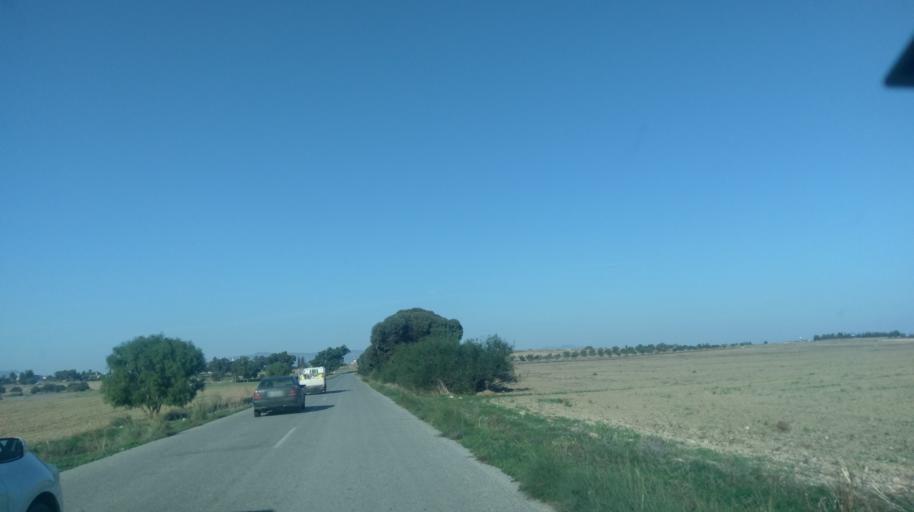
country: CY
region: Ammochostos
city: Lefkonoiko
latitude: 35.2083
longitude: 33.6968
